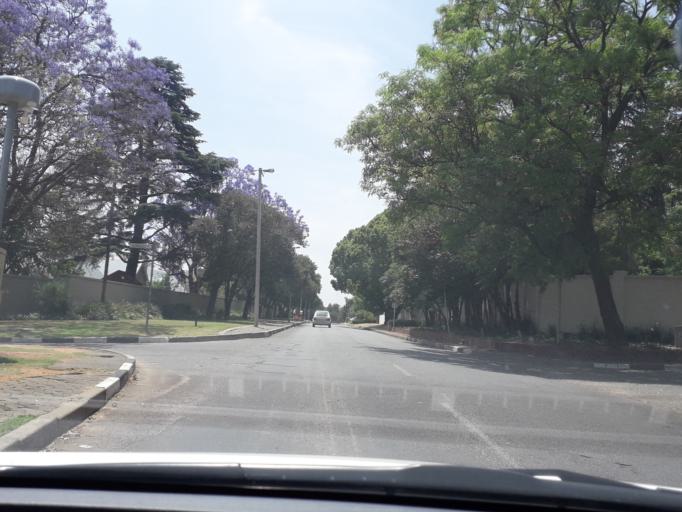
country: ZA
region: Gauteng
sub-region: City of Johannesburg Metropolitan Municipality
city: Johannesburg
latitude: -26.1080
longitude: 28.0264
